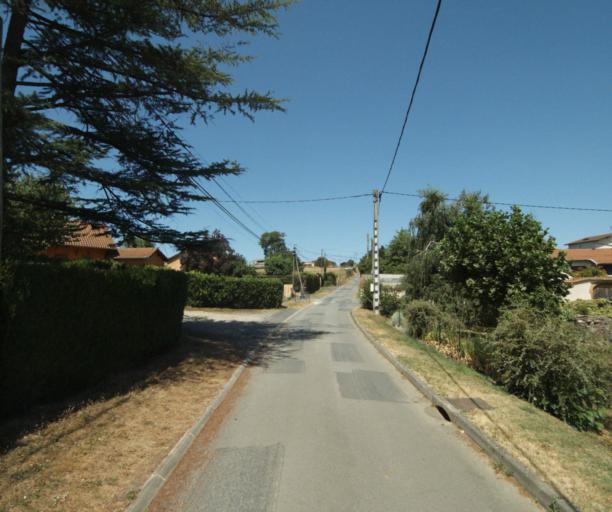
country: FR
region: Rhone-Alpes
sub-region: Departement du Rhone
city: Bessenay
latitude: 45.7578
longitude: 4.5459
